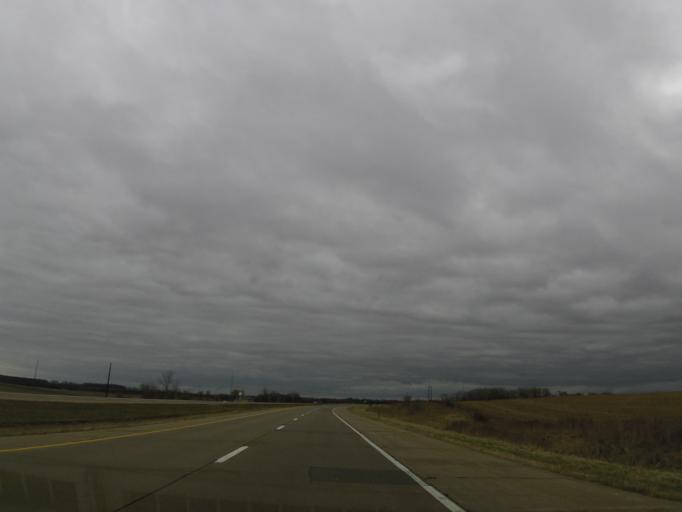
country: US
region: Iowa
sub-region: Buchanan County
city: Jesup
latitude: 42.3305
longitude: -92.0028
